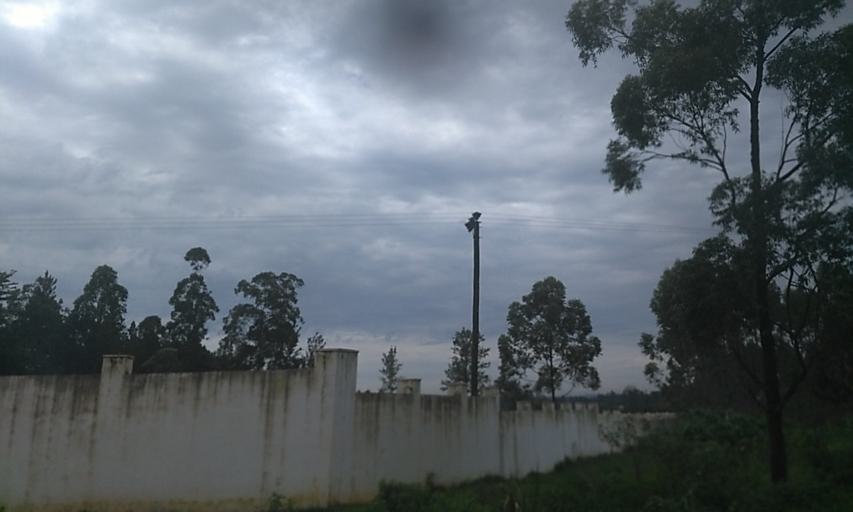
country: UG
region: Central Region
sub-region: Wakiso District
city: Bweyogerere
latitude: 0.3969
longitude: 32.6764
